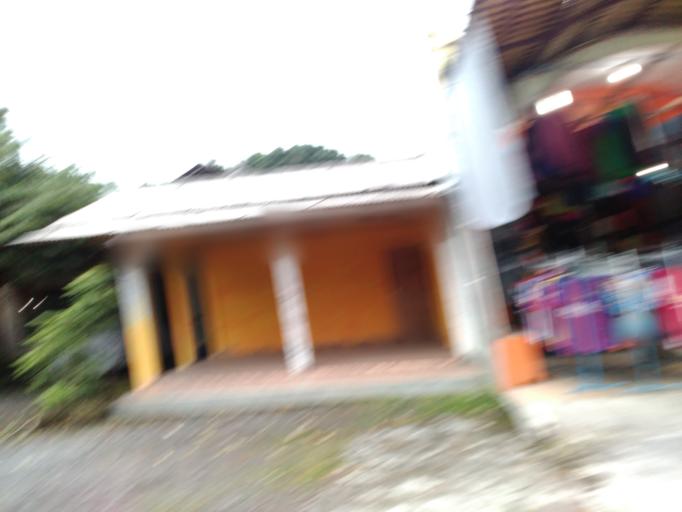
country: ID
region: Central Java
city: Boyolali
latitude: -7.5282
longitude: 110.5998
